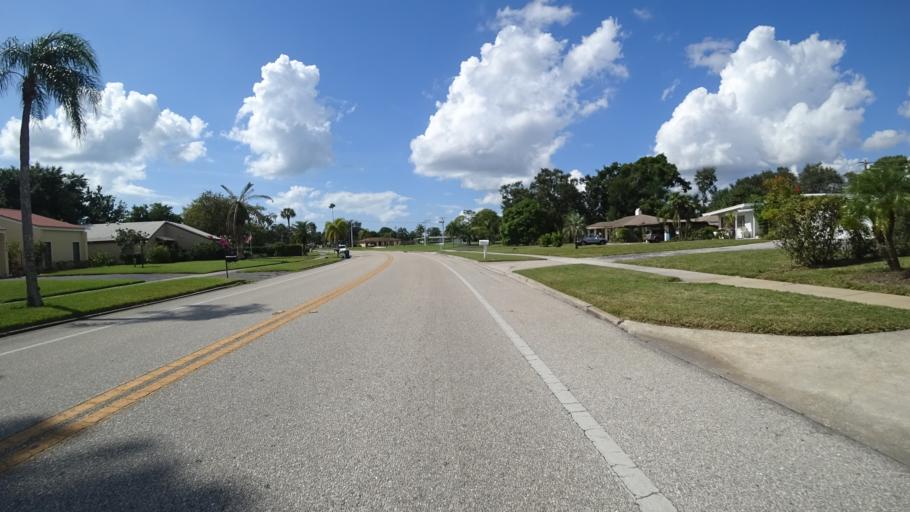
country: US
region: Florida
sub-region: Manatee County
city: Whitfield
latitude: 27.4139
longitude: -82.5656
